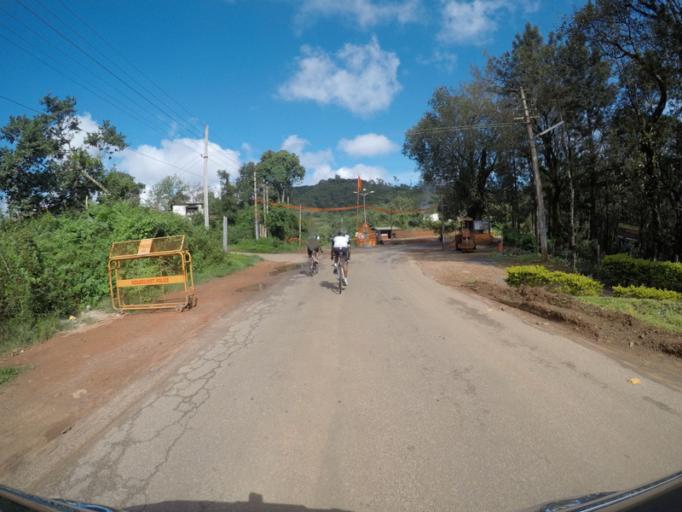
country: IN
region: Karnataka
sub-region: Kodagu
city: Madikeri
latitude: 12.4328
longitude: 75.7519
